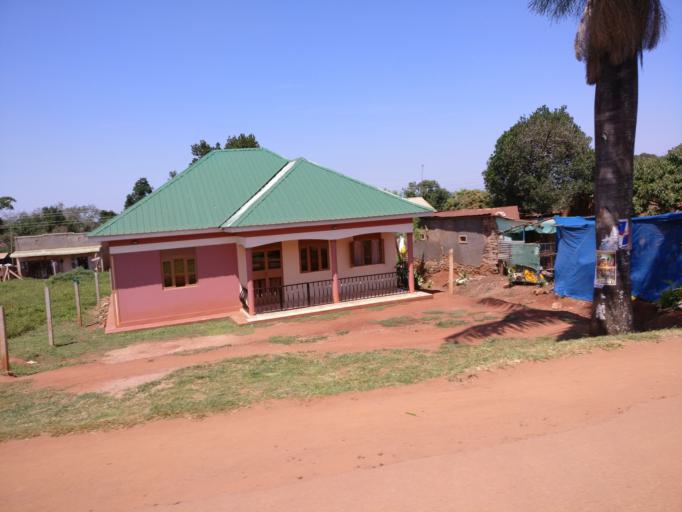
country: UG
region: Central Region
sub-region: Wakiso District
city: Entebbe
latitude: 0.1063
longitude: 32.5199
